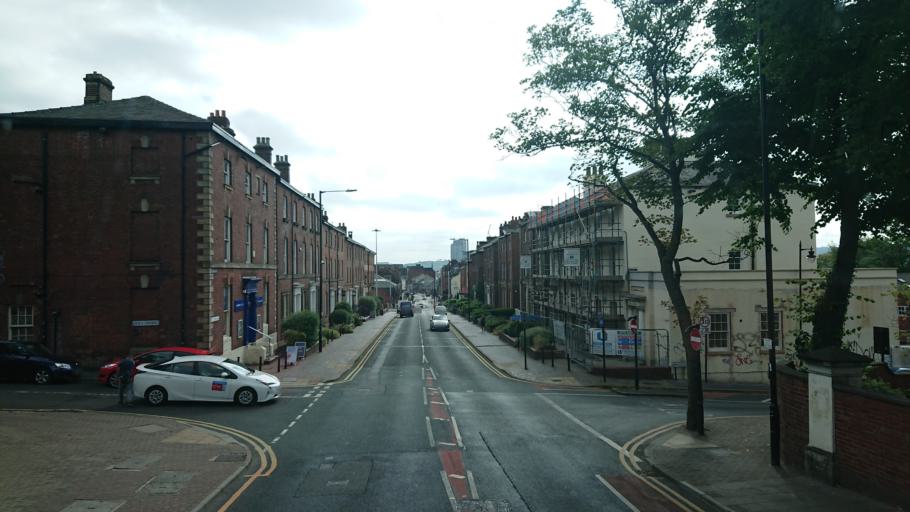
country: GB
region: England
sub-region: Sheffield
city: Sheffield
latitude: 53.3803
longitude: -1.4867
